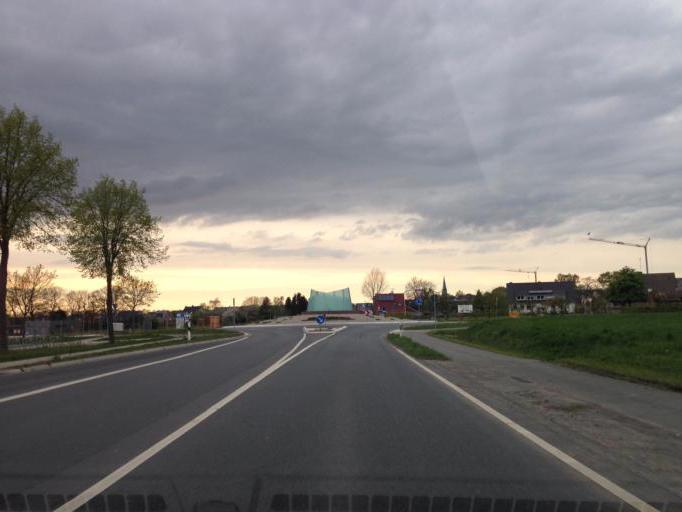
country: DE
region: North Rhine-Westphalia
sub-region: Regierungsbezirk Munster
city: Altenberge
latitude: 52.0371
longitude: 7.4757
